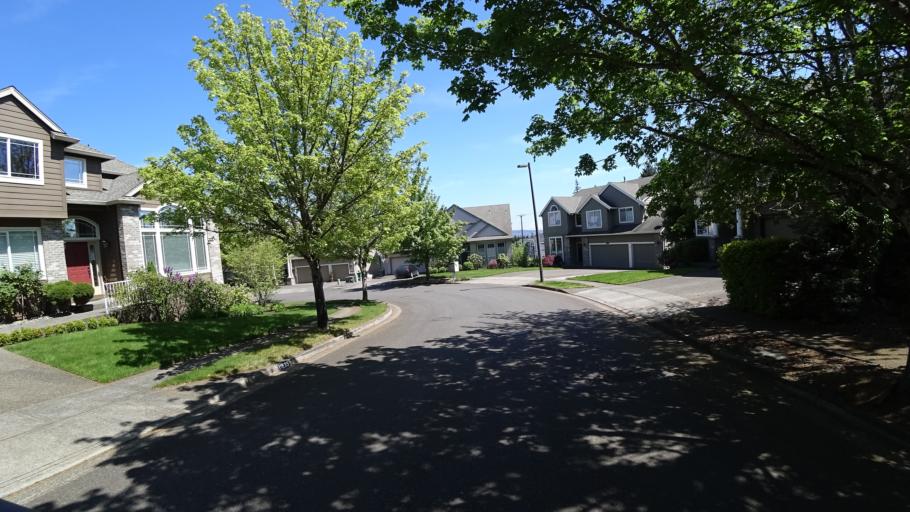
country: US
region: Oregon
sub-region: Washington County
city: King City
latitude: 45.4336
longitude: -122.8387
